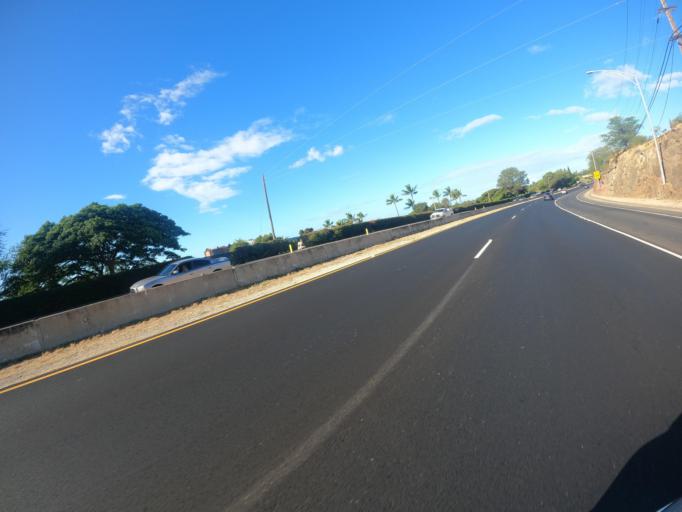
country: US
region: Hawaii
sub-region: Honolulu County
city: Makakilo City
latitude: 21.3444
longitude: -158.1194
